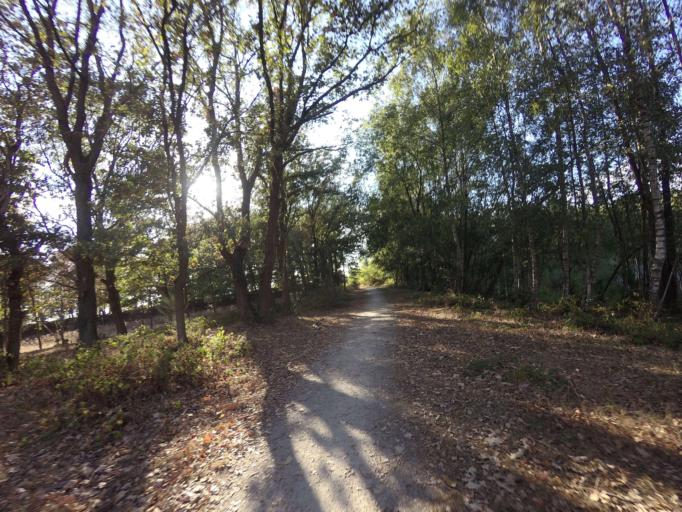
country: NL
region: North Brabant
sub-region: Gemeente Mill en Sint Hubert
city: Wilbertoord
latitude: 51.6980
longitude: 5.7531
